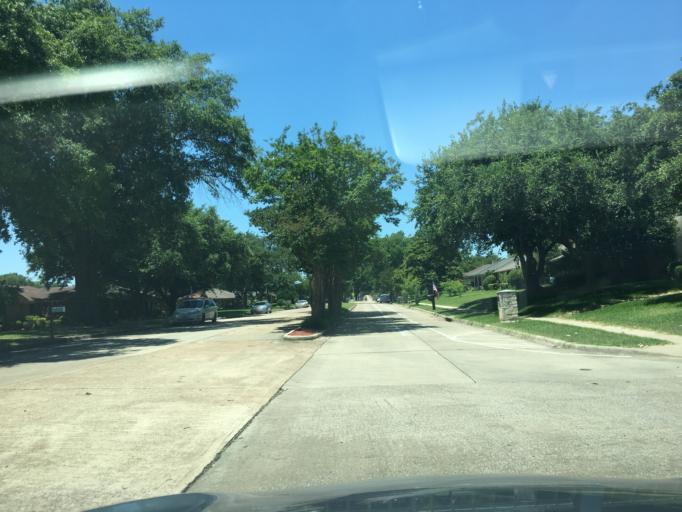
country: US
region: Texas
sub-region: Dallas County
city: Richardson
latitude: 32.9531
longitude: -96.6851
